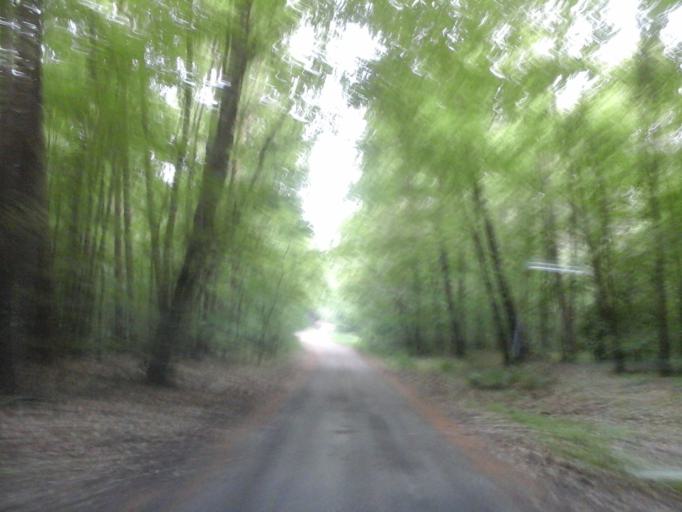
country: PL
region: West Pomeranian Voivodeship
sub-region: Powiat mysliborski
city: Barlinek
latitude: 52.9601
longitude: 15.2880
